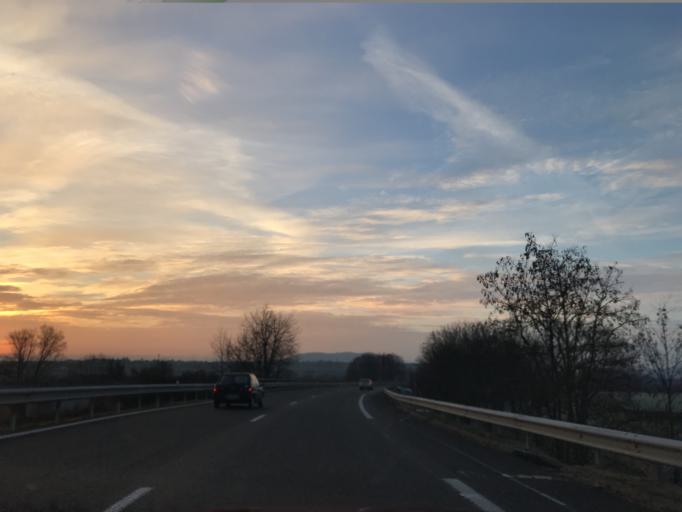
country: FR
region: Auvergne
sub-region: Departement du Puy-de-Dome
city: Pont-du-Chateau
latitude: 45.8261
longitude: 3.2237
